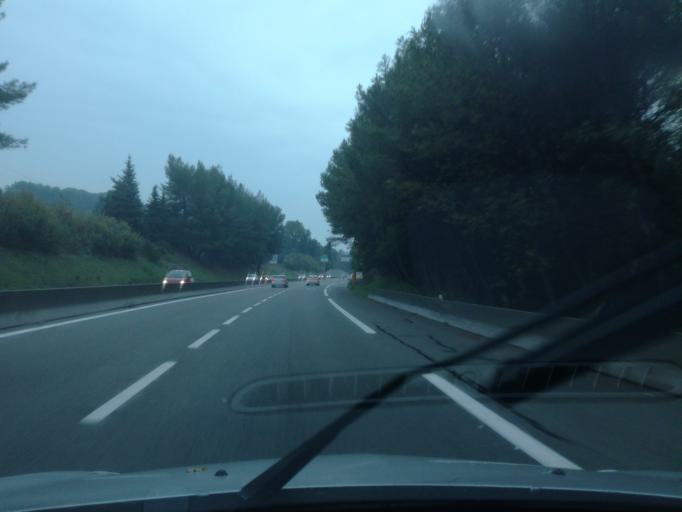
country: FR
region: Provence-Alpes-Cote d'Azur
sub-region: Departement des Alpes-Maritimes
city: Mougins
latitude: 43.5951
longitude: 7.0001
